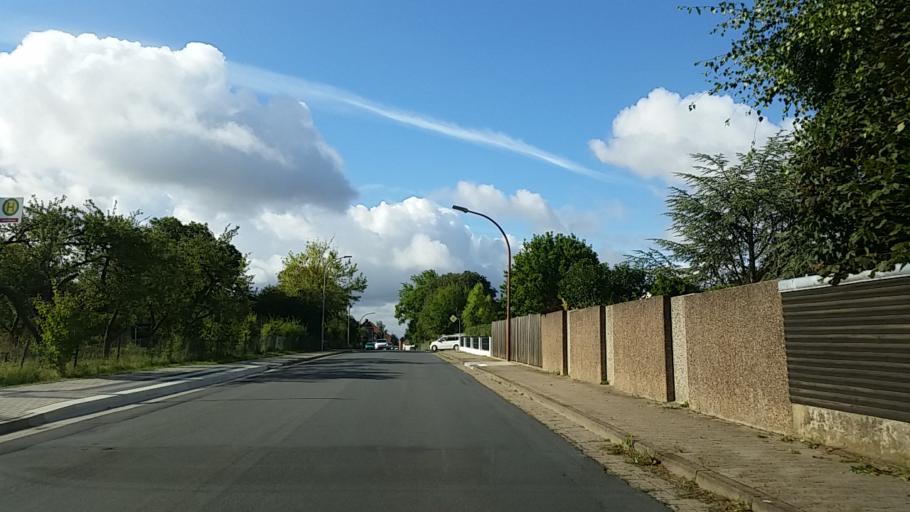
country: DE
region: Lower Saxony
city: Sickte
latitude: 52.2217
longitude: 10.6441
